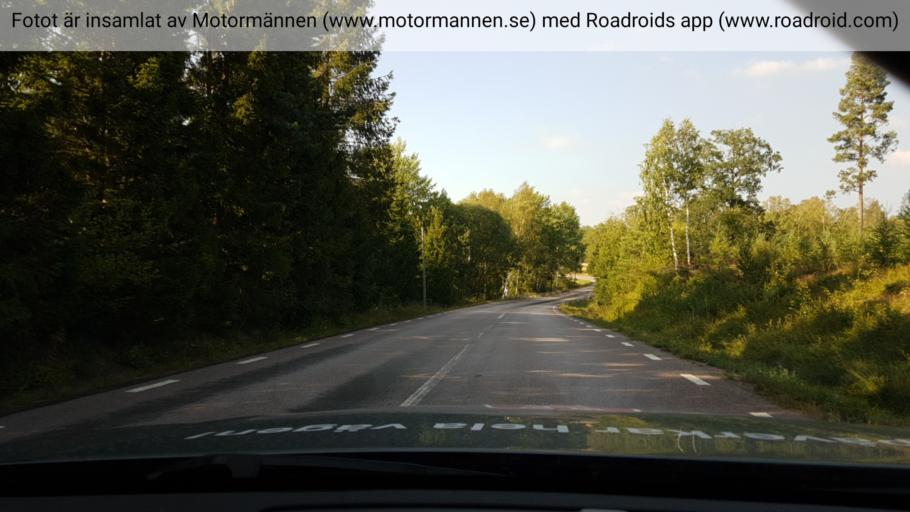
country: SE
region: Soedermanland
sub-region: Strangnas Kommun
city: Mariefred
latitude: 59.2014
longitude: 17.1921
